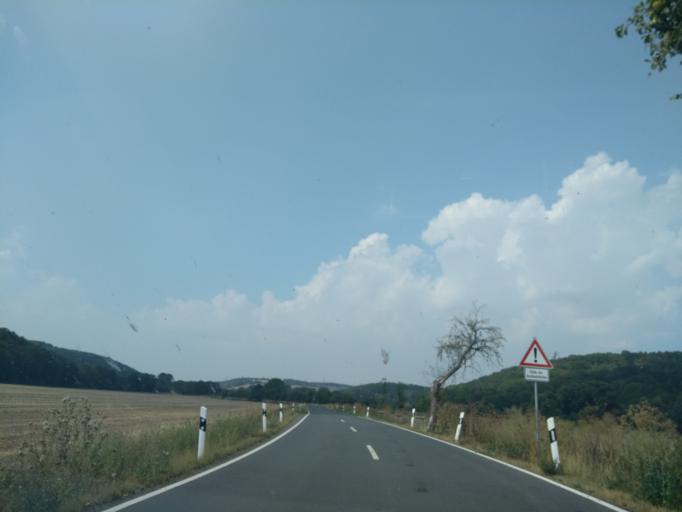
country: DE
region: Saxony-Anhalt
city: Kretzschau
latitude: 51.0266
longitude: 12.0719
